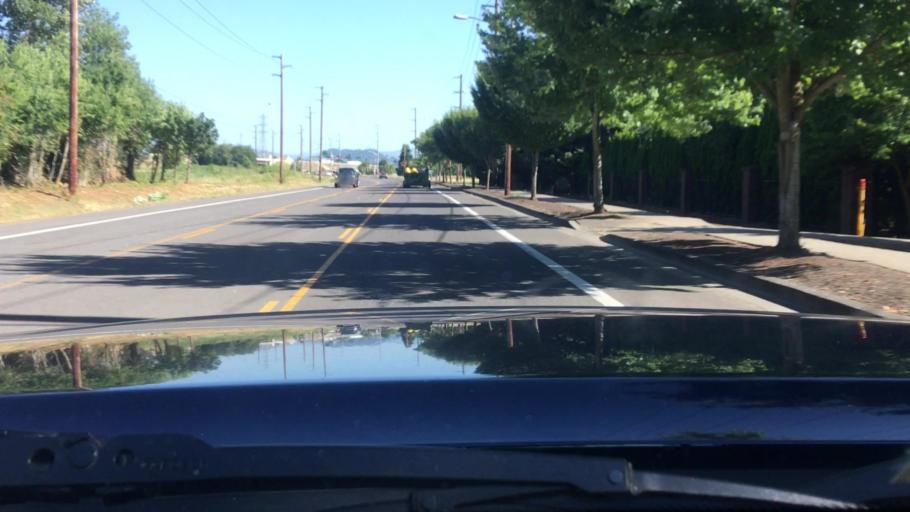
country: US
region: Oregon
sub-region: Lane County
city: Coburg
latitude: 44.0936
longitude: -123.0508
